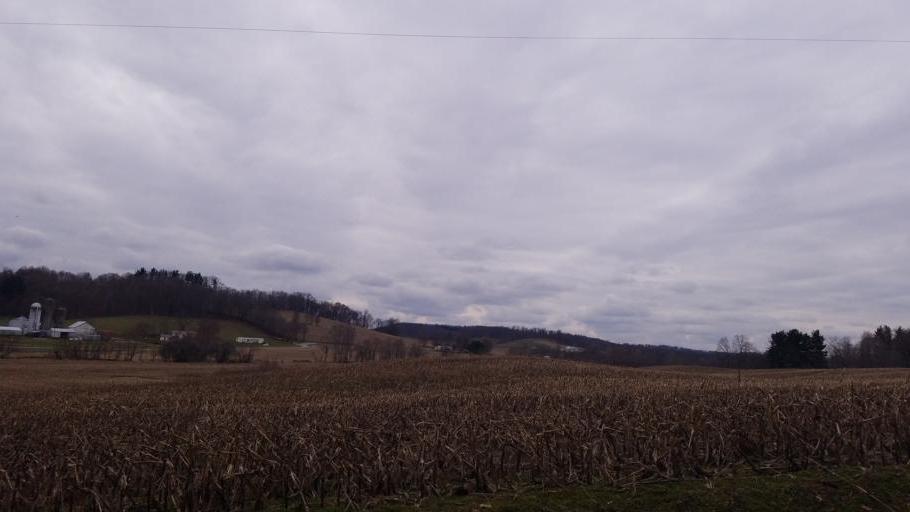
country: US
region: Ohio
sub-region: Sandusky County
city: Bellville
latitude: 40.6000
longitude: -82.4845
